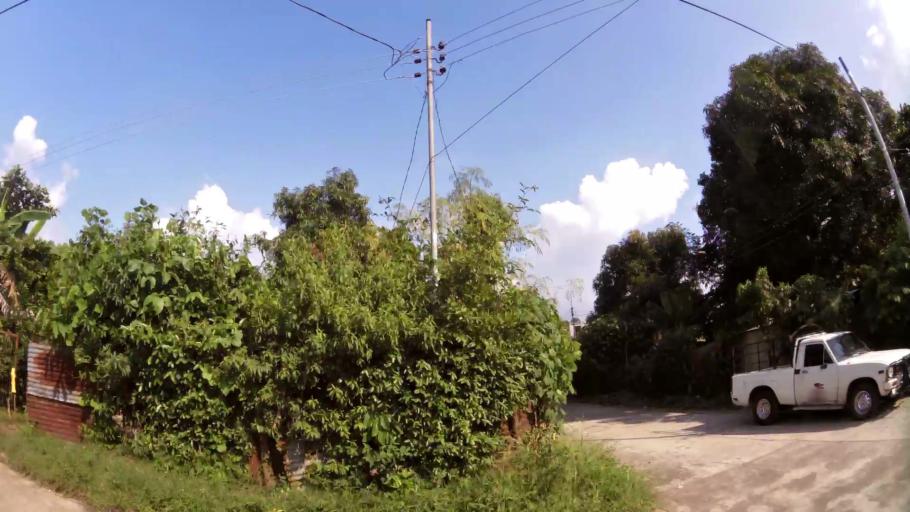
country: GT
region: Retalhuleu
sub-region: Municipio de Retalhuleu
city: Retalhuleu
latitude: 14.5386
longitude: -91.6928
